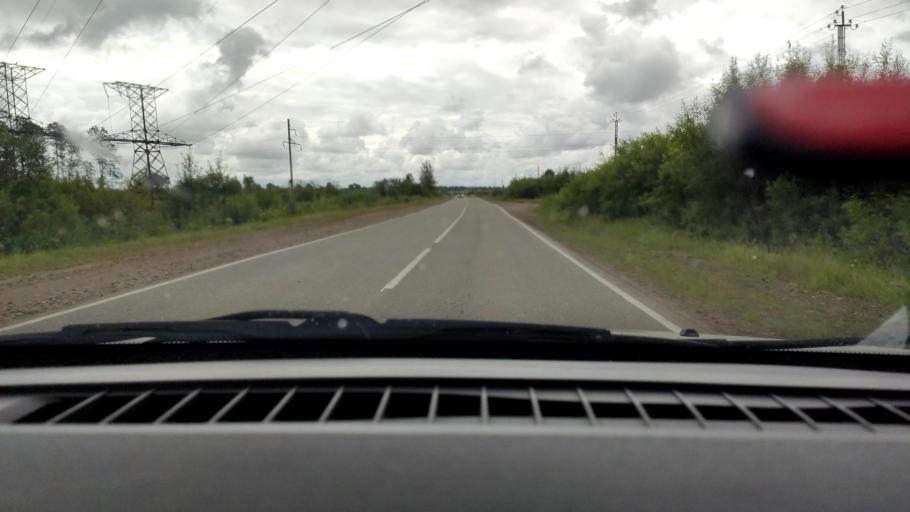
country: RU
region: Perm
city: Chaykovskaya
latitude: 58.0853
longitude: 55.6140
